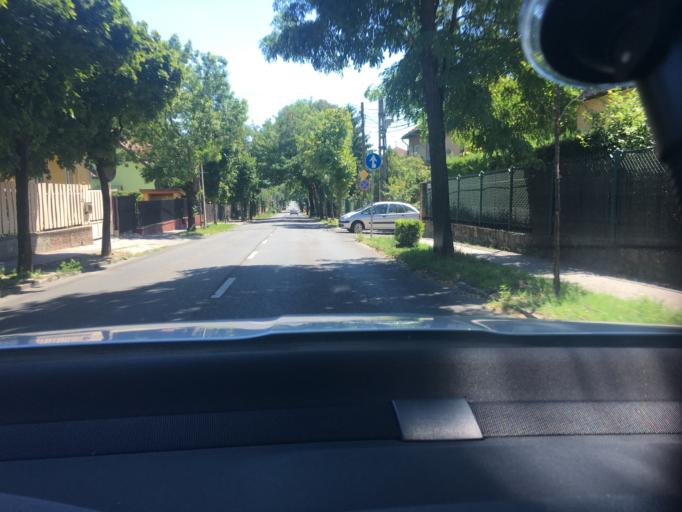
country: HU
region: Budapest
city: Budapest XVI. keruelet
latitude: 47.5157
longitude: 19.1717
